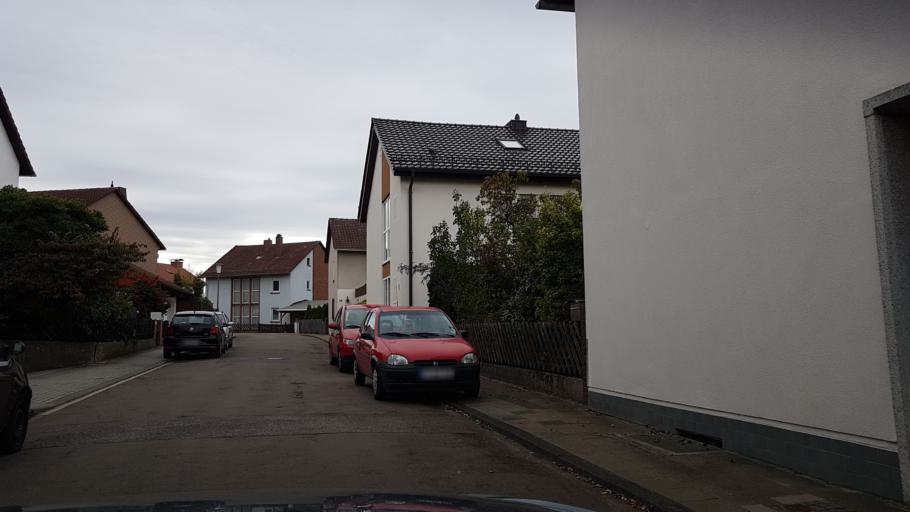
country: DE
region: Rheinland-Pfalz
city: Zweibrucken
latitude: 49.2442
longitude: 7.3802
